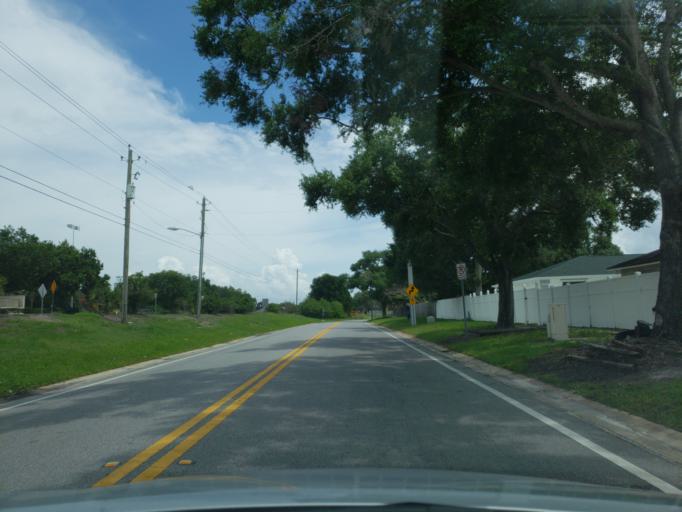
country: US
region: Florida
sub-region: Hillsborough County
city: Town 'n' Country
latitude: 28.0287
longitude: -82.5501
